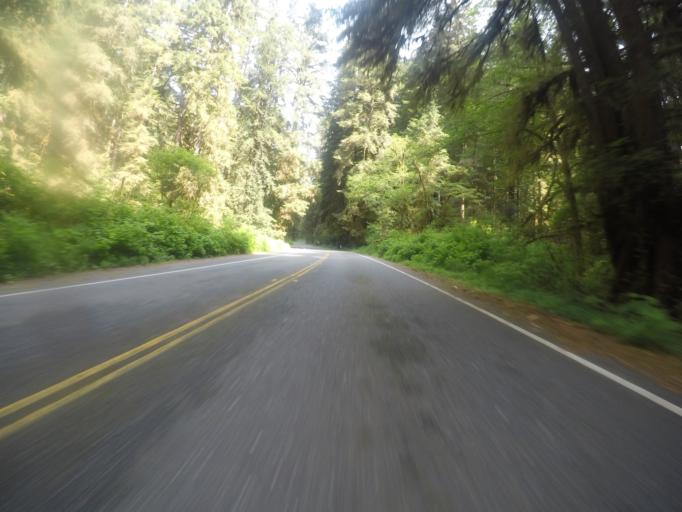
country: US
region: California
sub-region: Del Norte County
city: Bertsch-Oceanview
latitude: 41.4336
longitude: -124.0386
